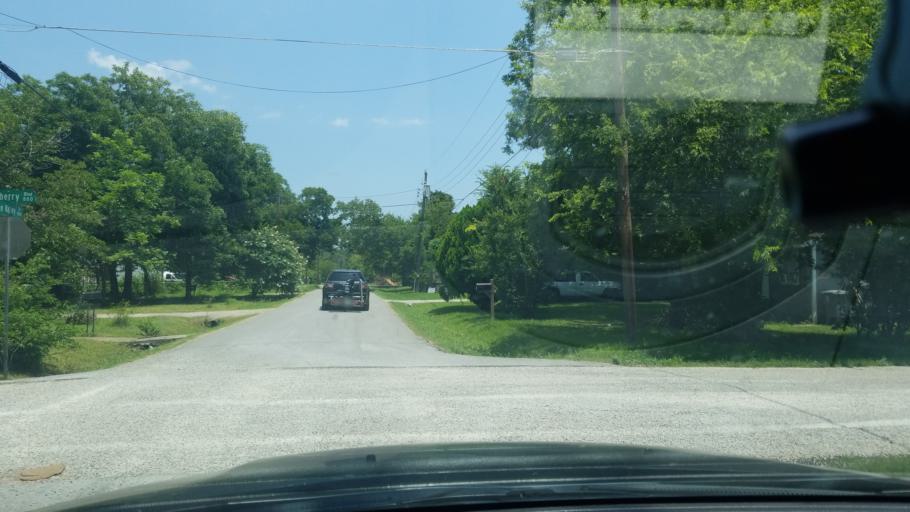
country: US
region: Texas
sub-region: Dallas County
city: Balch Springs
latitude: 32.7253
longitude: -96.6683
